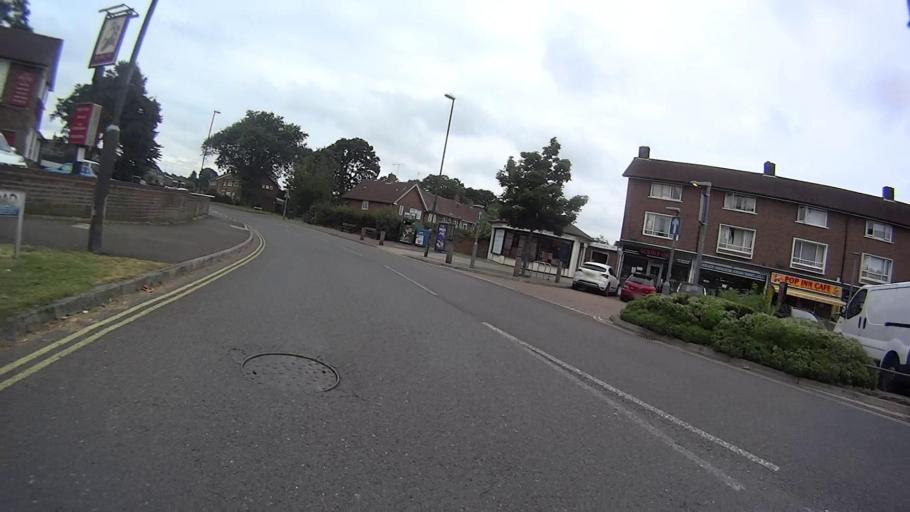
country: GB
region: England
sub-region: West Sussex
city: Langley Green
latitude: 51.1188
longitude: -0.1993
